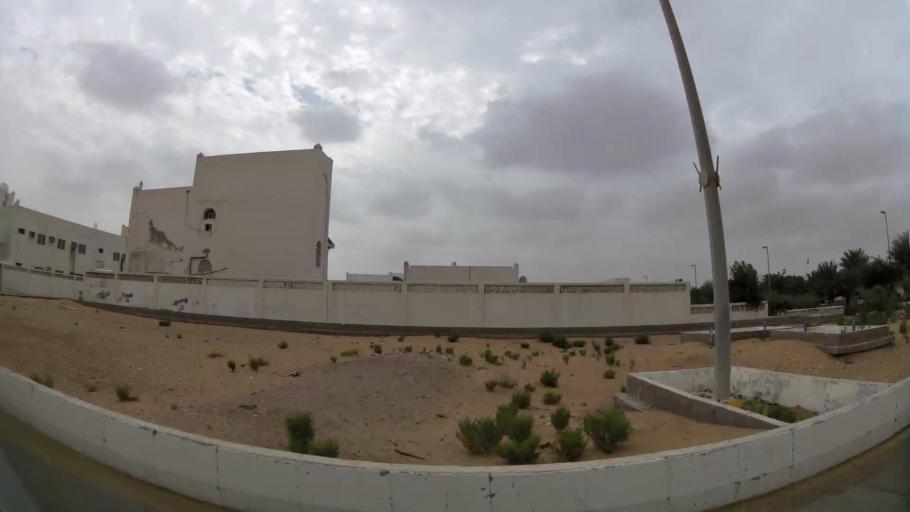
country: AE
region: Abu Dhabi
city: Abu Dhabi
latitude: 24.3455
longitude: 54.6449
